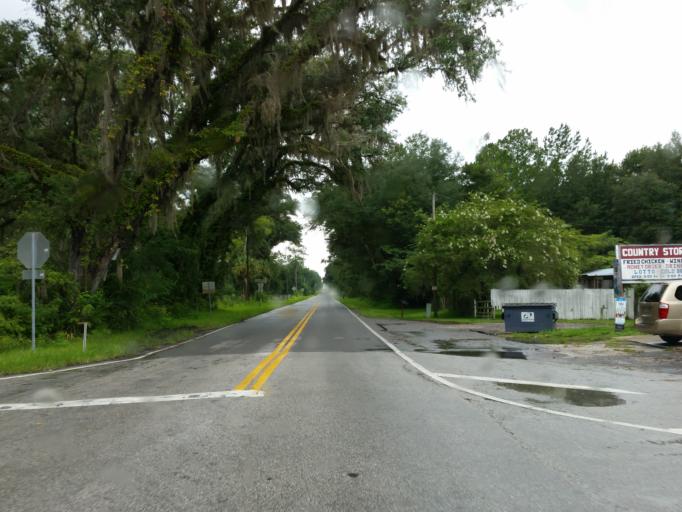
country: US
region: Florida
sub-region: Levy County
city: Williston
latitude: 29.4077
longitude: -82.2978
